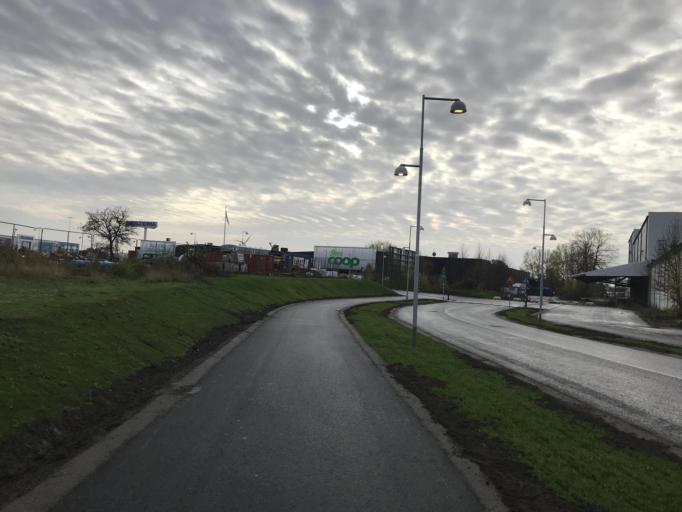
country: SE
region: Skane
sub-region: Landskrona
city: Landskrona
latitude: 55.8754
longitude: 12.8569
